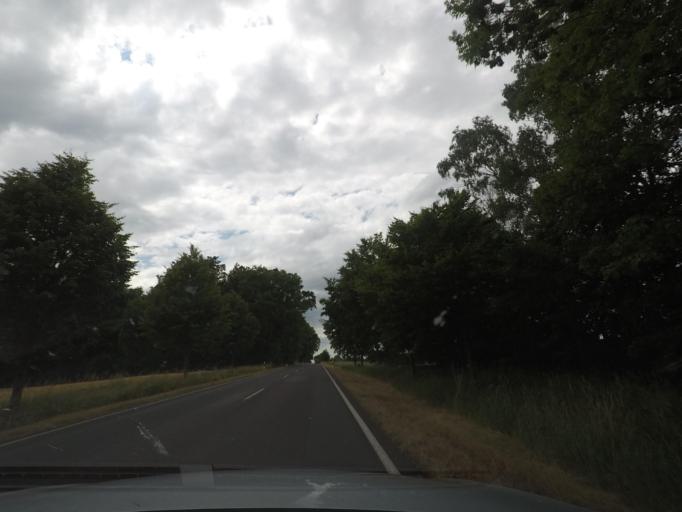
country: DE
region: Saxony-Anhalt
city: Hotensleben
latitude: 52.1048
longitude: 11.0583
